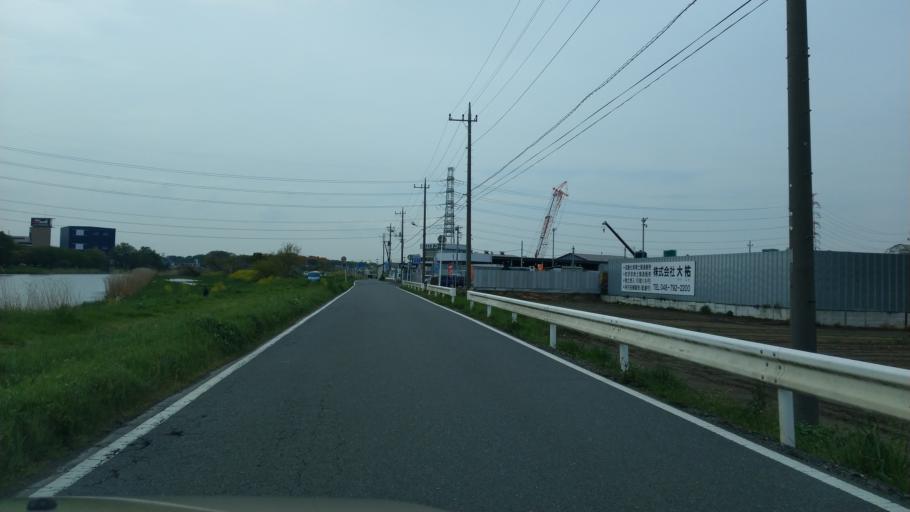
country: JP
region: Saitama
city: Iwatsuki
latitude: 35.9461
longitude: 139.7237
